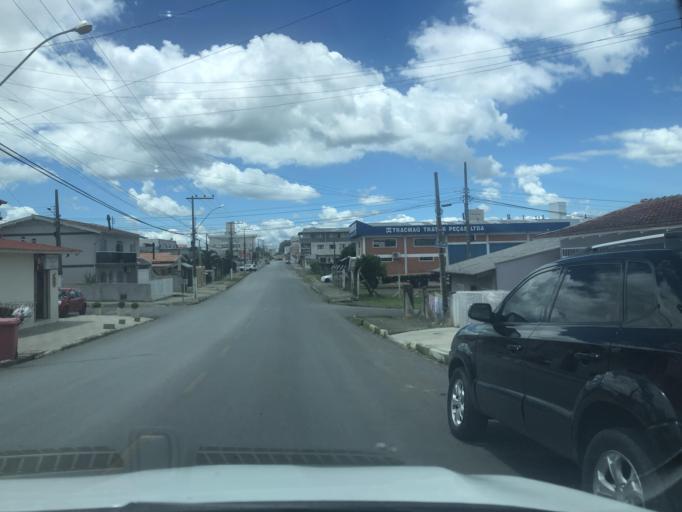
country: BR
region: Santa Catarina
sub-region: Lages
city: Lages
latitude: -27.8019
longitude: -50.3019
